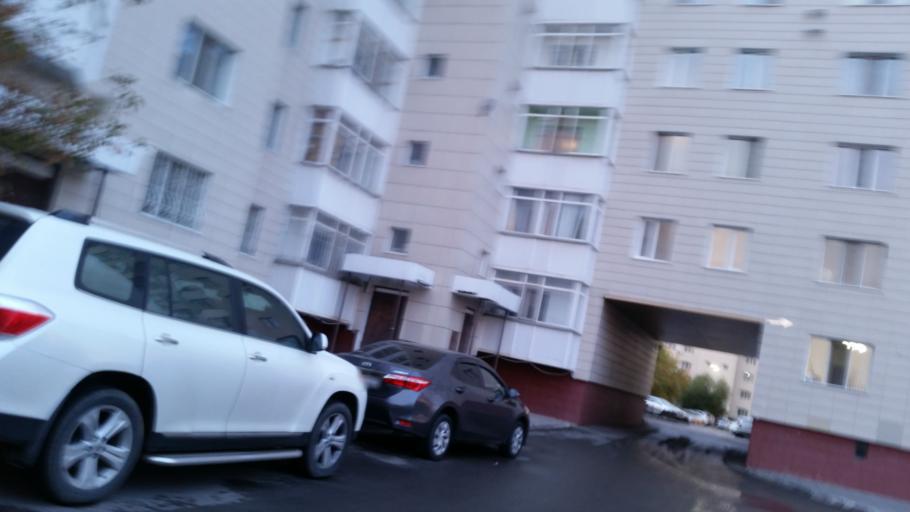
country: KZ
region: Astana Qalasy
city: Astana
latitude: 51.1201
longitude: 71.4194
